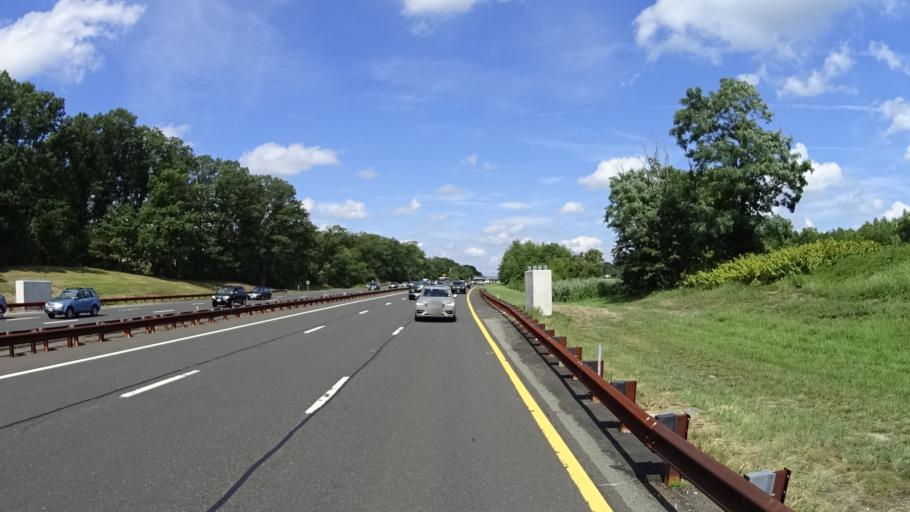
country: US
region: New Jersey
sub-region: Monmouth County
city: Matawan
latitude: 40.4312
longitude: -74.2464
